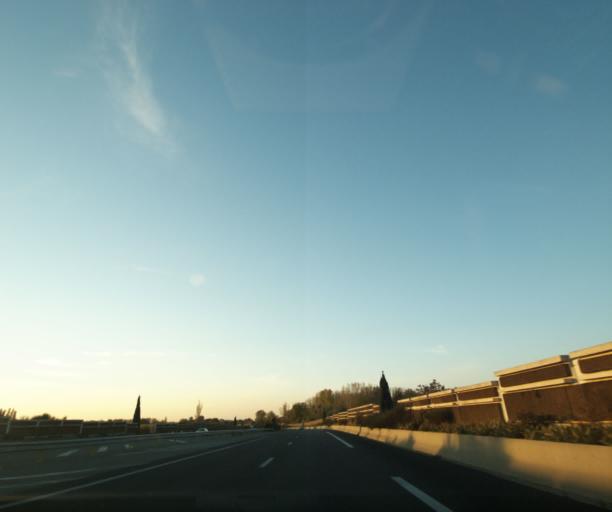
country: FR
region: Provence-Alpes-Cote d'Azur
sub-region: Departement des Bouches-du-Rhone
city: Grans
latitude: 43.6264
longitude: 5.0719
